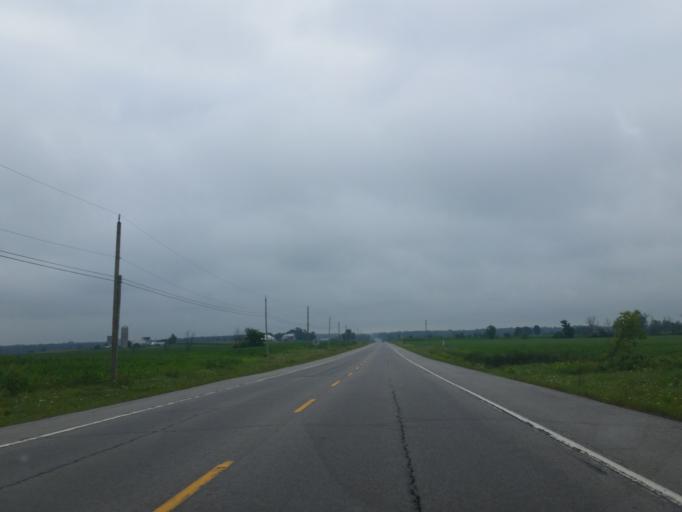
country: CA
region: Ontario
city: Clarence-Rockland
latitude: 45.4120
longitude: -75.4028
